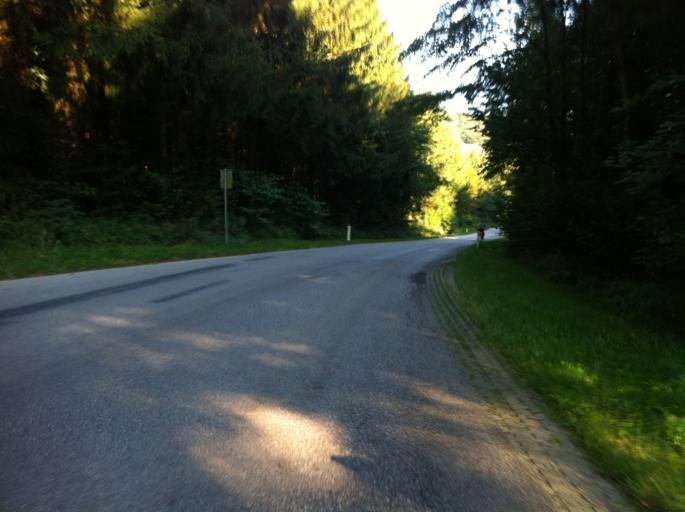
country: AT
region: Lower Austria
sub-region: Politischer Bezirk Wien-Umgebung
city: Pressbaum
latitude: 48.1988
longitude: 16.1162
